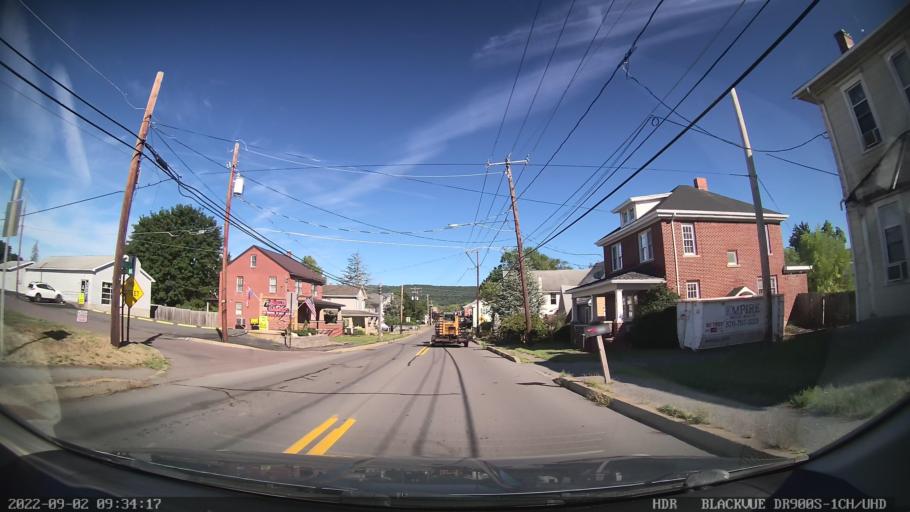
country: US
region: Pennsylvania
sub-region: Northumberland County
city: Elysburg
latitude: 40.8636
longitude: -76.5512
